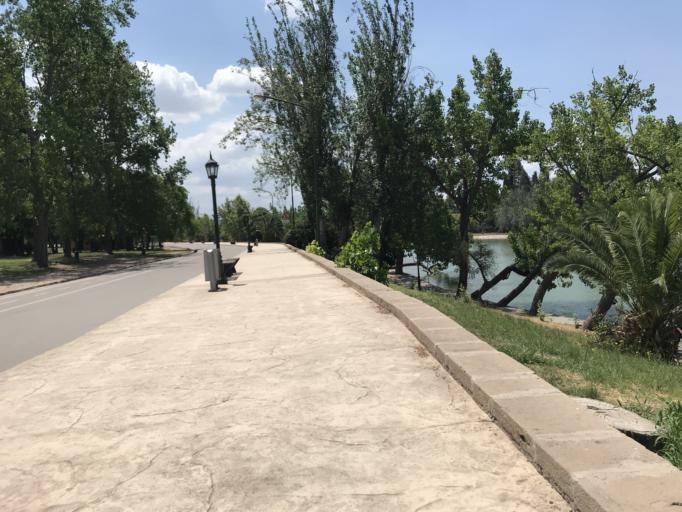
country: AR
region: Mendoza
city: Mendoza
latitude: -32.8964
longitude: -68.8654
